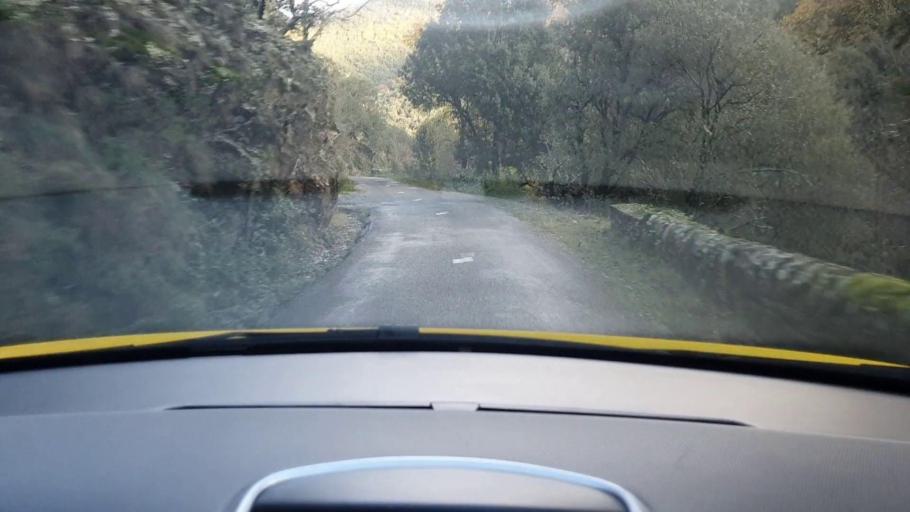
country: FR
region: Languedoc-Roussillon
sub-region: Departement du Gard
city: Valleraugue
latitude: 44.0975
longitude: 3.7333
